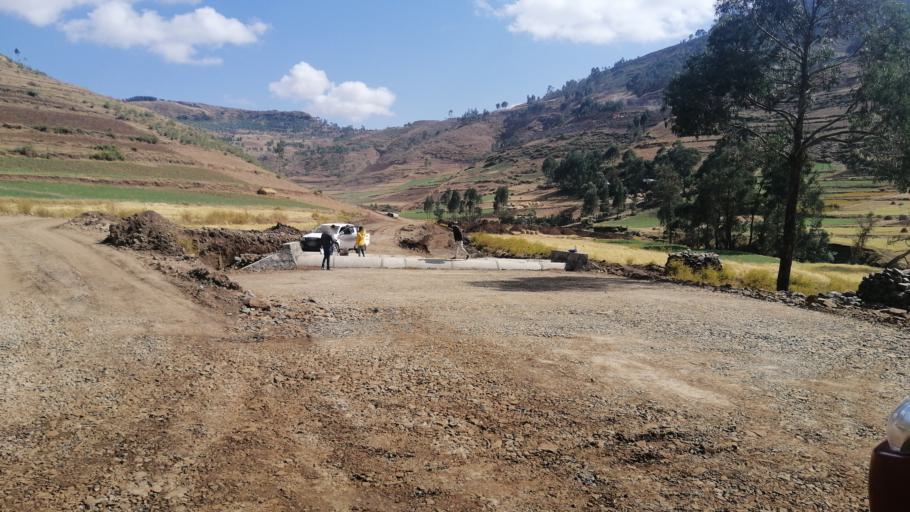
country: ET
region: Amhara
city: Debre Tabor
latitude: 11.4159
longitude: 38.2039
